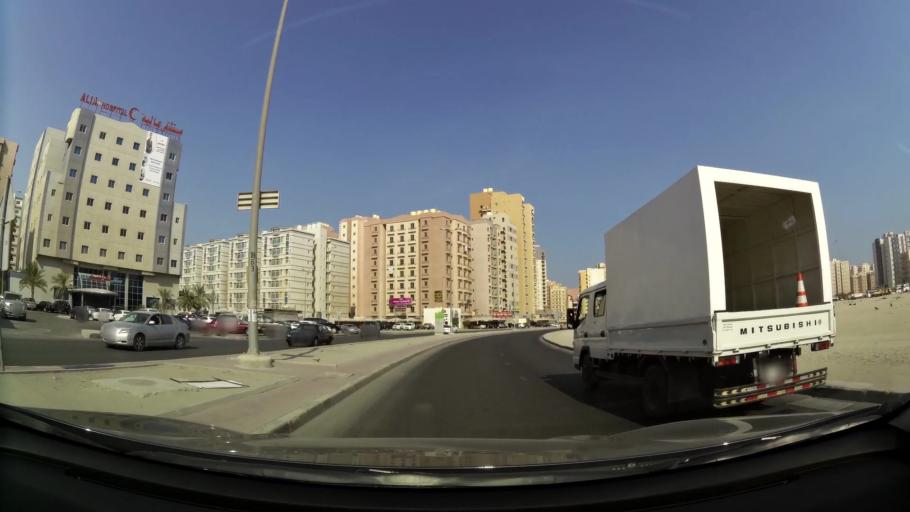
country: KW
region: Al Ahmadi
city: Al Mahbulah
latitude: 29.1447
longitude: 48.1208
